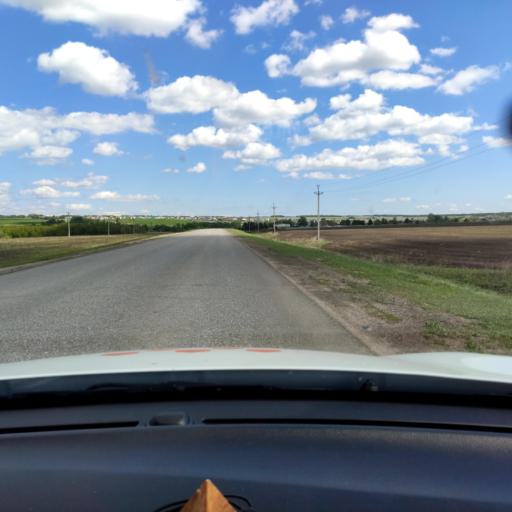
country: RU
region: Tatarstan
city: Kuybyshevskiy Zaton
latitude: 55.1711
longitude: 49.2204
